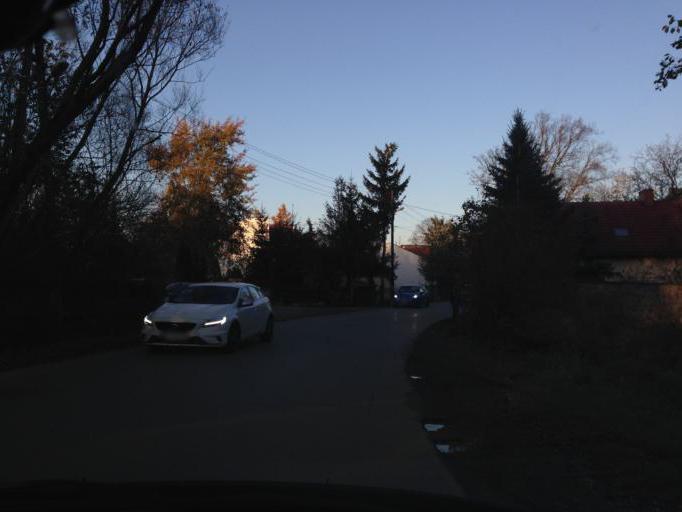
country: PL
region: Lesser Poland Voivodeship
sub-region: Powiat krakowski
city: Rzaska
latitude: 50.0745
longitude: 19.8775
